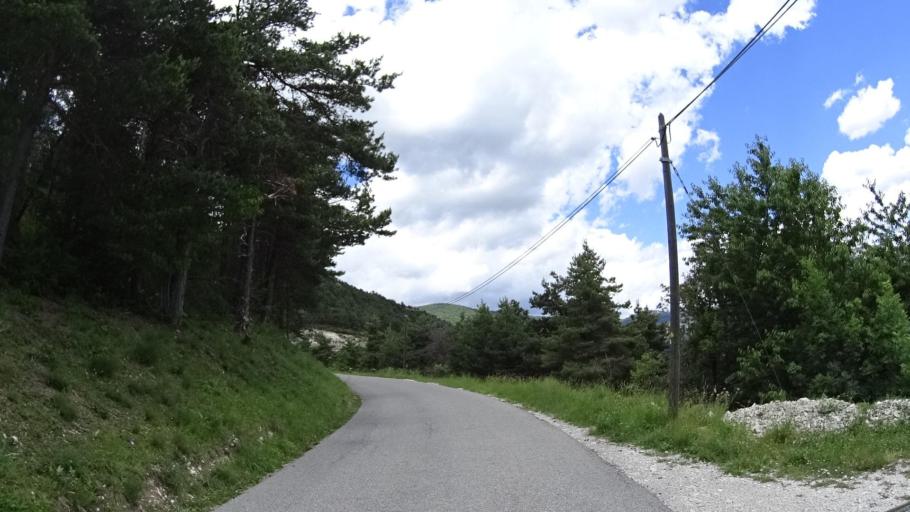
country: FR
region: Provence-Alpes-Cote d'Azur
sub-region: Departement des Alpes-de-Haute-Provence
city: Annot
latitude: 44.0240
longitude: 6.6193
